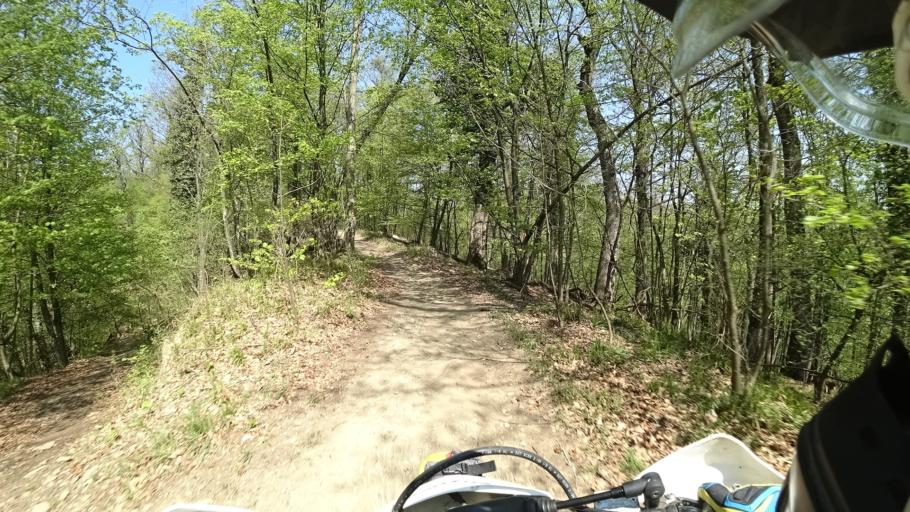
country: HR
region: Zagrebacka
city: Jablanovec
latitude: 45.8705
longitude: 15.9025
